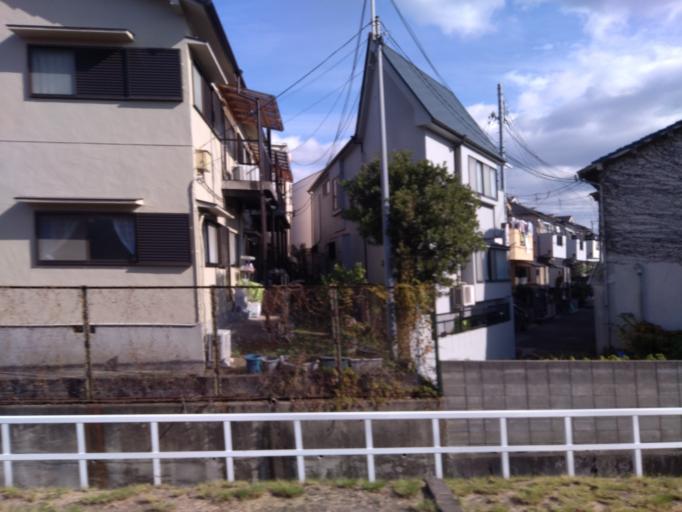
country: JP
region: Osaka
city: Ikeda
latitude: 34.8030
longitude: 135.4466
